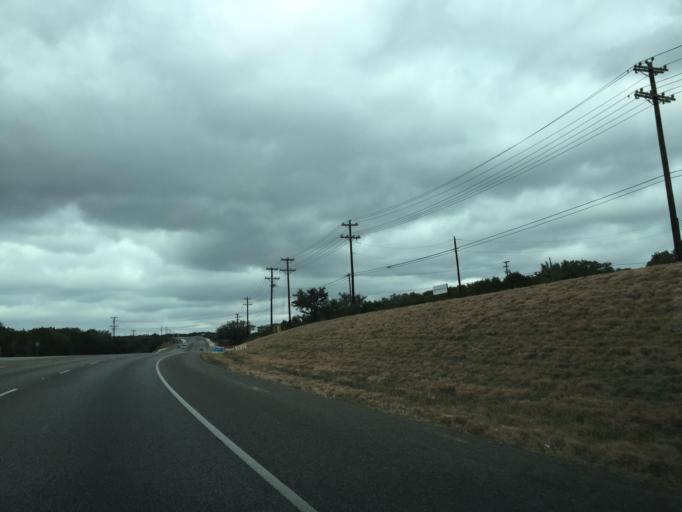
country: US
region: Texas
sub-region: Travis County
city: The Hills
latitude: 30.3406
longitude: -98.0421
